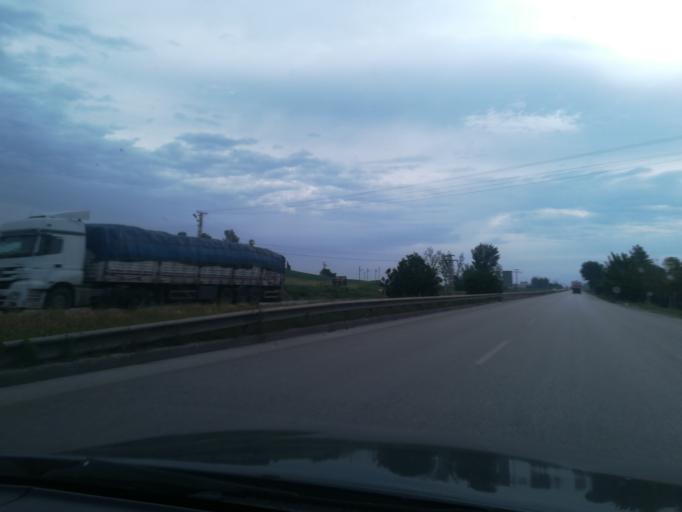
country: TR
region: Adana
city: Ceyhan
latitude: 37.0521
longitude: 35.8366
